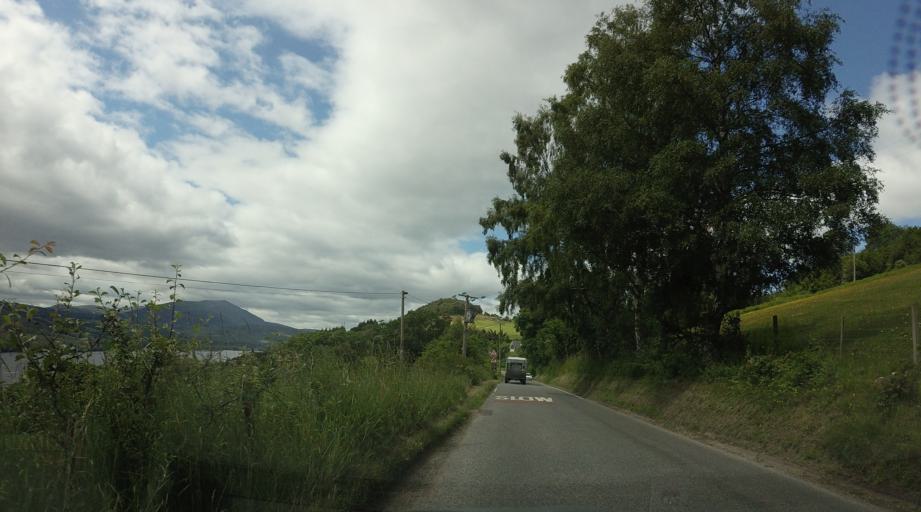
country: GB
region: Scotland
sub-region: Perth and Kinross
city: Aberfeldy
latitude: 56.7181
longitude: -3.9286
